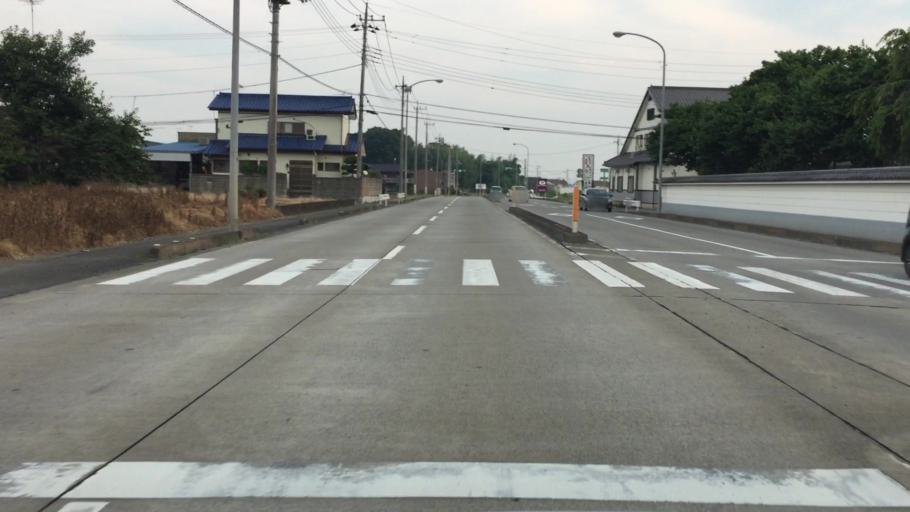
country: JP
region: Tochigi
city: Tochigi
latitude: 36.3364
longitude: 139.6950
